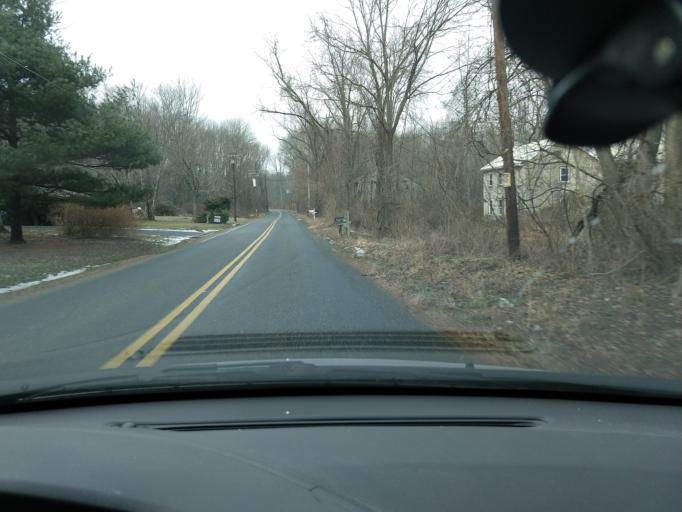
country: US
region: Pennsylvania
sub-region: Berks County
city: Birdsboro
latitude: 40.2433
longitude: -75.7705
